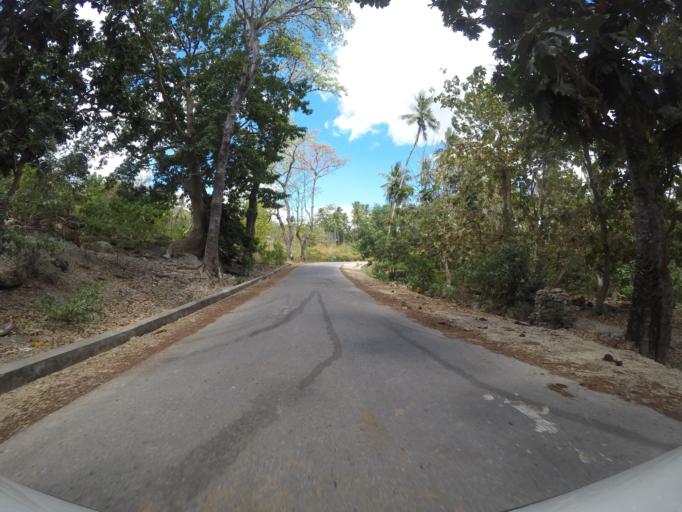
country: TL
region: Lautem
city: Lospalos
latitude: -8.3572
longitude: 126.9303
